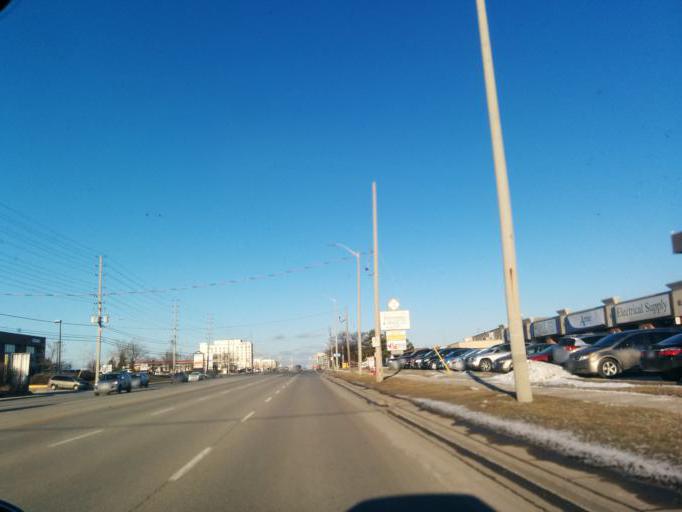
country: CA
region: Ontario
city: Etobicoke
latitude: 43.6336
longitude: -79.6230
